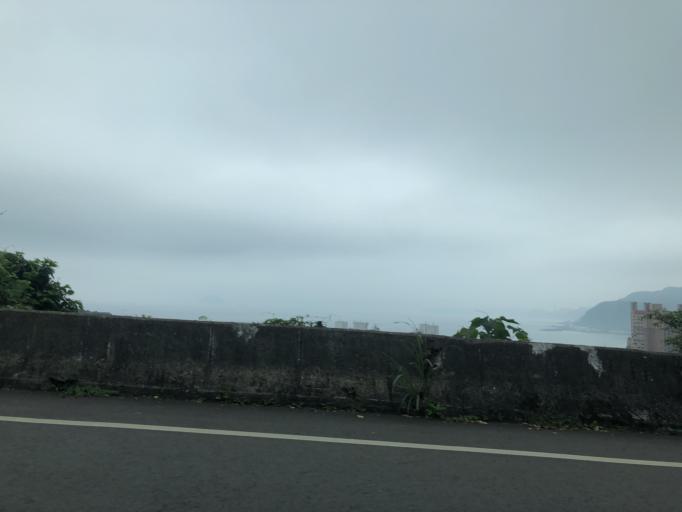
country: TW
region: Taiwan
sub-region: Keelung
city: Keelung
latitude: 25.1918
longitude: 121.6799
